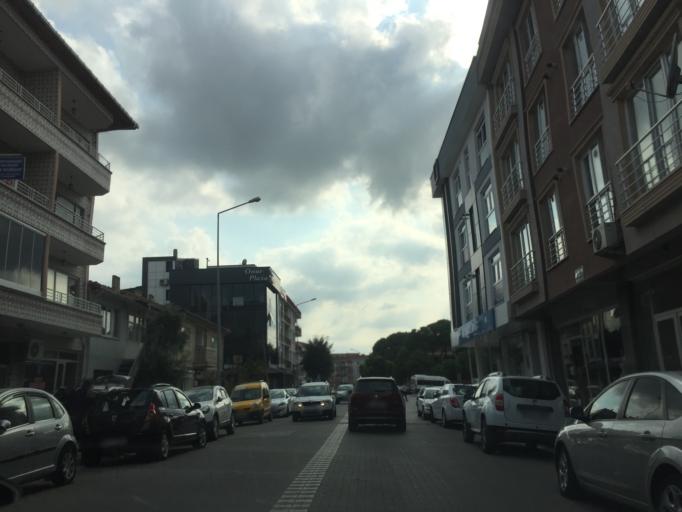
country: TR
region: Balikesir
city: Gonen
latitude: 40.1051
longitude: 27.6542
